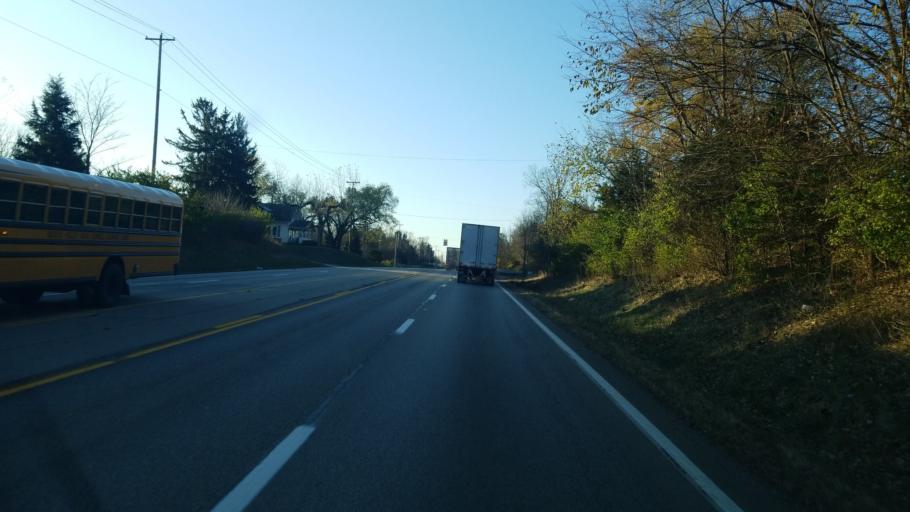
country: US
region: Ohio
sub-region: Delaware County
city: Delaware
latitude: 40.3551
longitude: -83.0740
